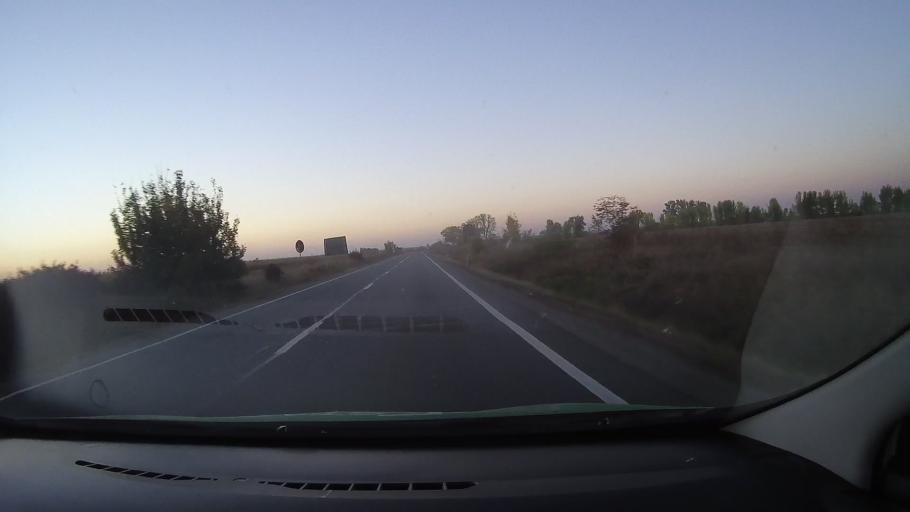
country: RO
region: Bihor
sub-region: Comuna Tarcea
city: Tarcea
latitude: 47.4317
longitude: 22.2064
